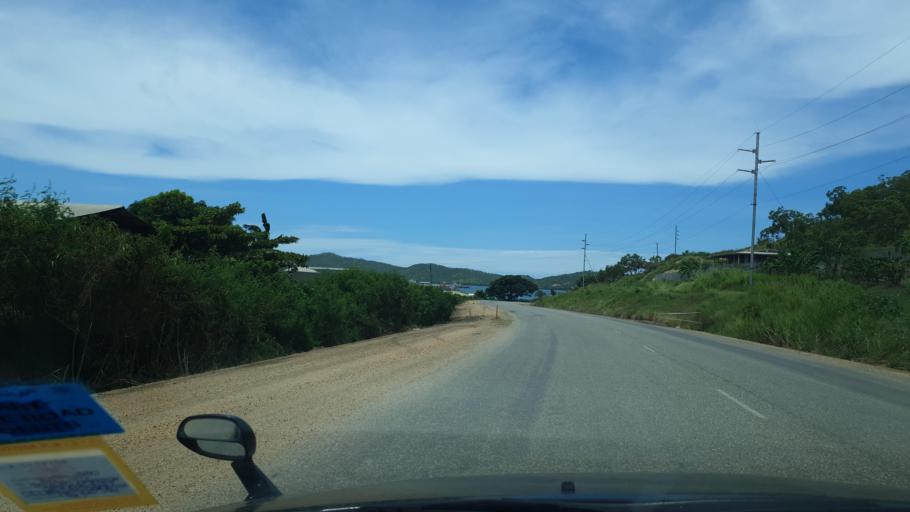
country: PG
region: National Capital
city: Port Moresby
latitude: -9.4172
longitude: 147.0997
